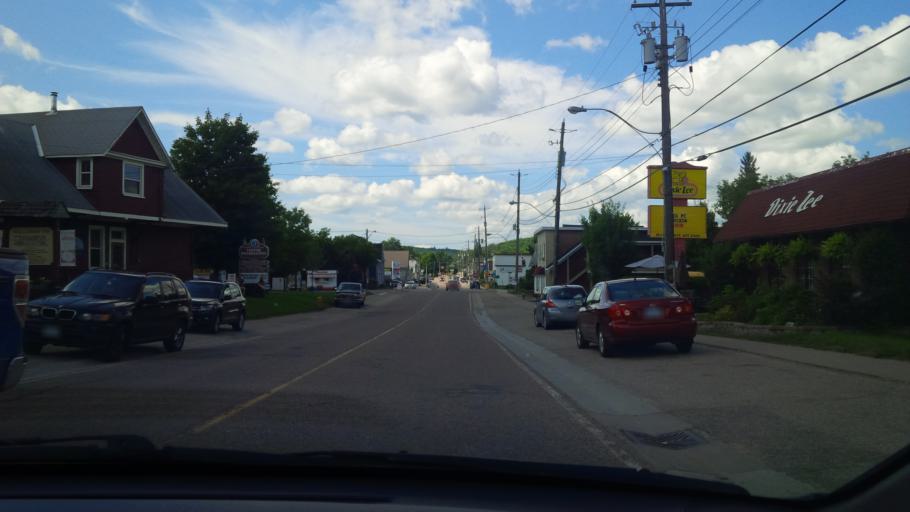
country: CA
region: Ontario
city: Bancroft
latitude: 45.4880
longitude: -77.6760
